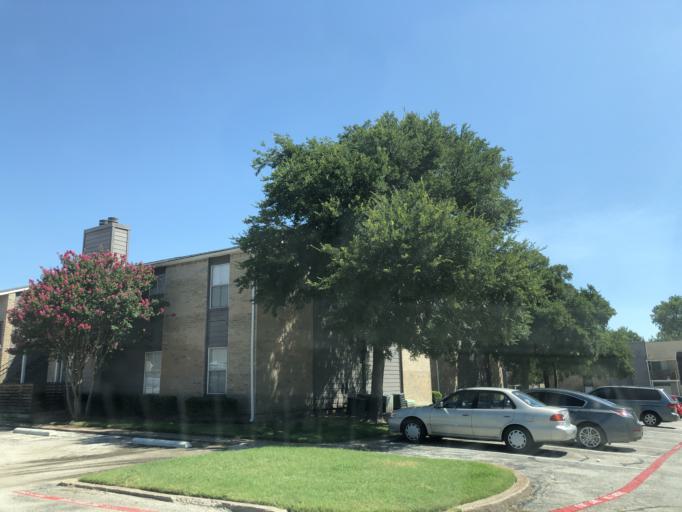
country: US
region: Texas
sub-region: Dallas County
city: Rowlett
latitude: 32.8512
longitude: -96.5968
